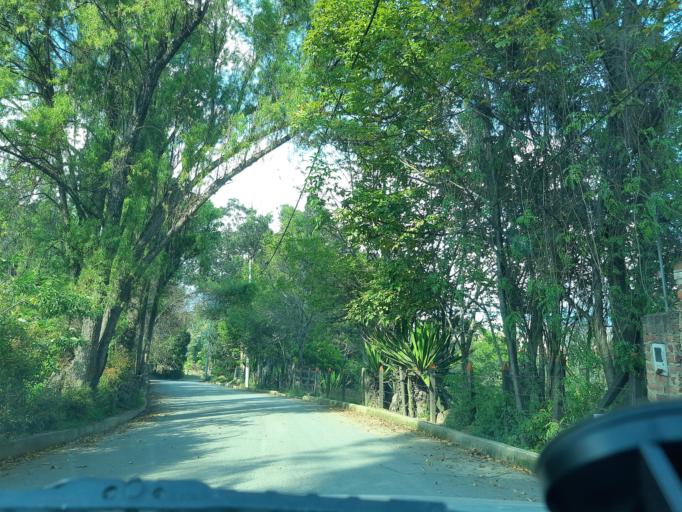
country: CO
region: Boyaca
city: Raquira
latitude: 5.5341
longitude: -73.6424
